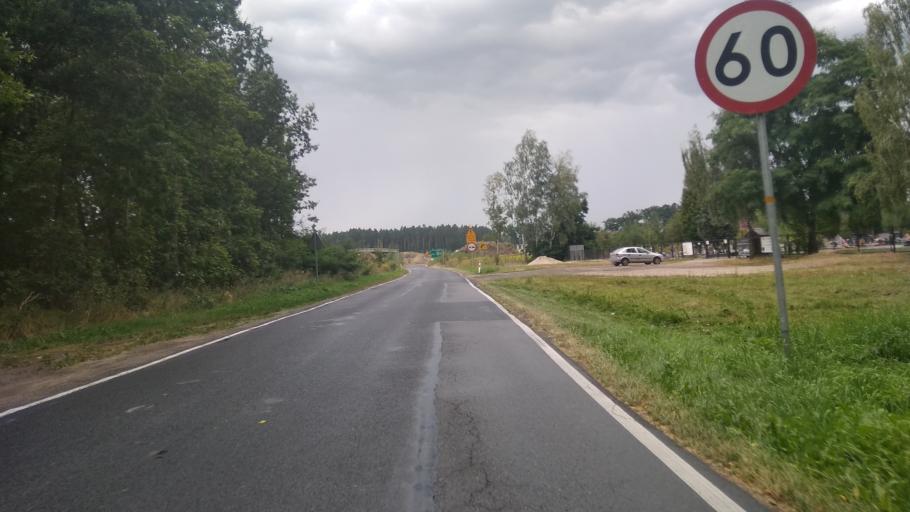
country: PL
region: Kujawsko-Pomorskie
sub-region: Powiat bydgoski
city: Osielsko
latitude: 53.2208
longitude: 18.1323
